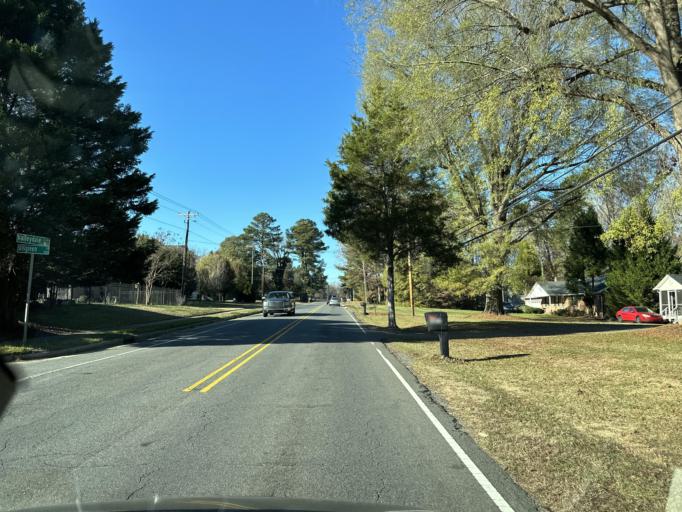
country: US
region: North Carolina
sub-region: Gaston County
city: Mount Holly
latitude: 35.2994
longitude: -80.9351
